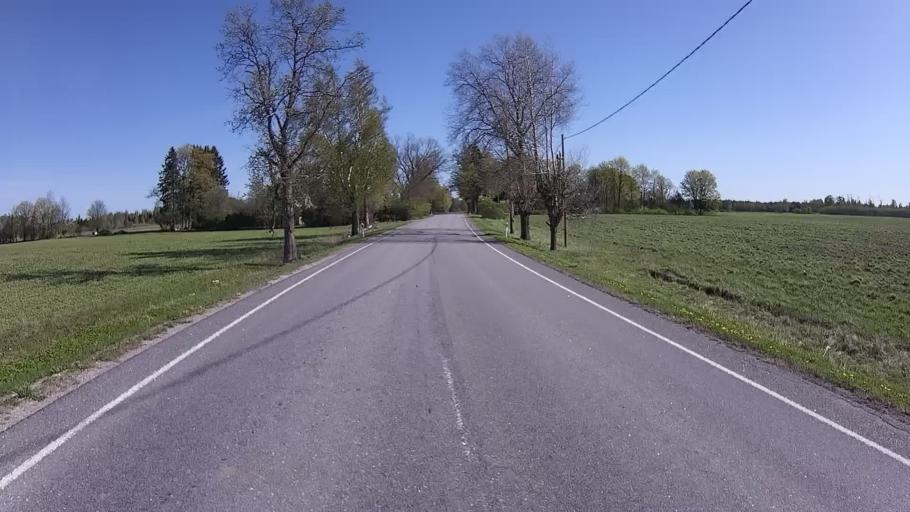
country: EE
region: Raplamaa
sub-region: Kehtna vald
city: Kehtna
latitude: 58.8840
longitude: 24.7823
